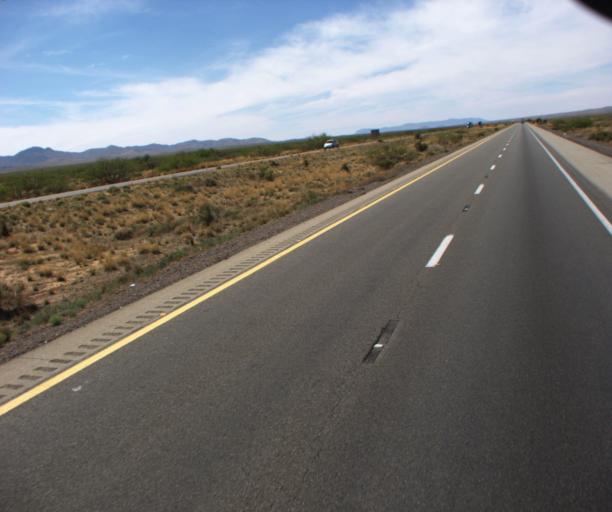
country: US
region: Arizona
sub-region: Cochise County
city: Willcox
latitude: 32.3407
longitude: -109.5629
